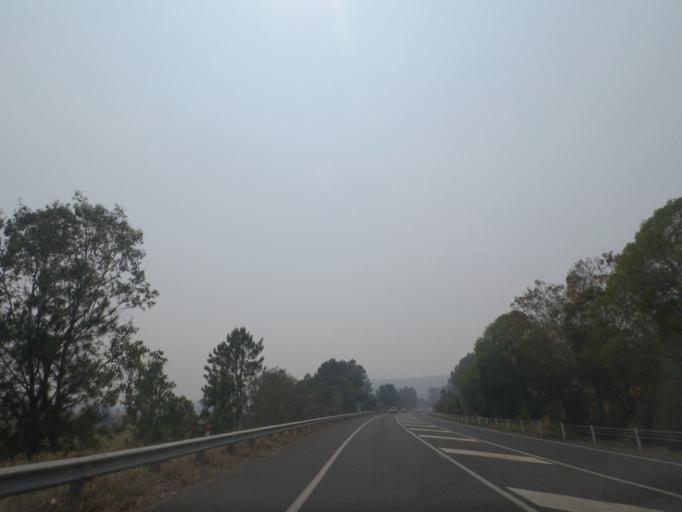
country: AU
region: New South Wales
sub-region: Clarence Valley
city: Maclean
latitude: -29.5649
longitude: 153.1404
